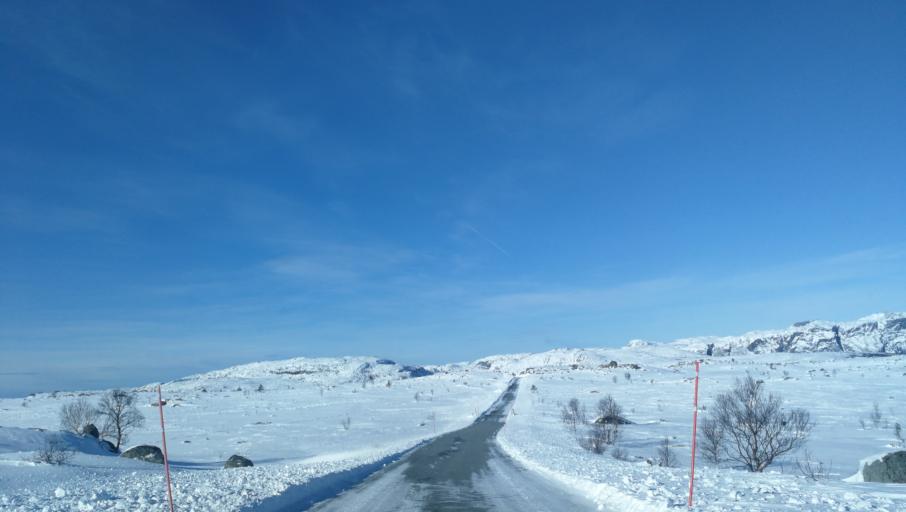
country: NO
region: Rogaland
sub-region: Hjelmeland
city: Hjelmelandsvagen
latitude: 59.1058
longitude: 6.3759
